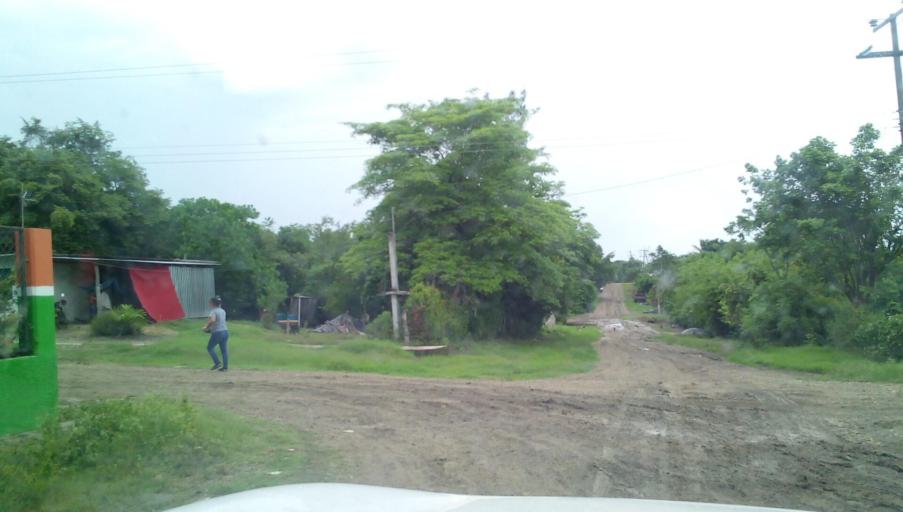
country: MX
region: Veracruz
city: Panuco
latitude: 21.8007
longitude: -98.1019
